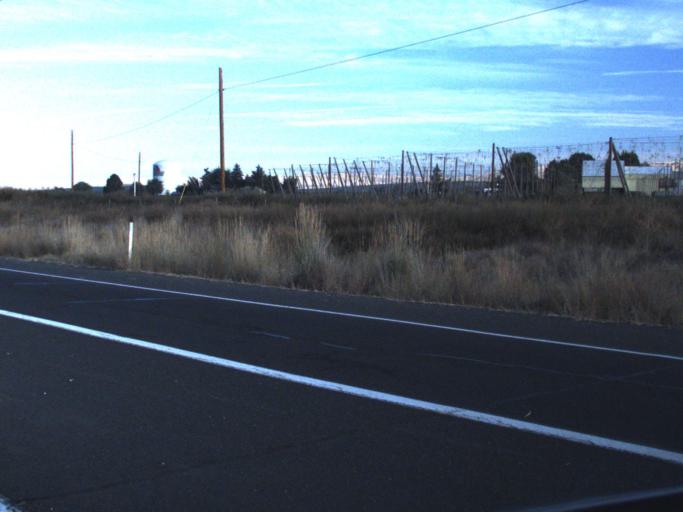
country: US
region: Washington
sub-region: Yakima County
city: Grandview
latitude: 46.2583
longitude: -119.8833
